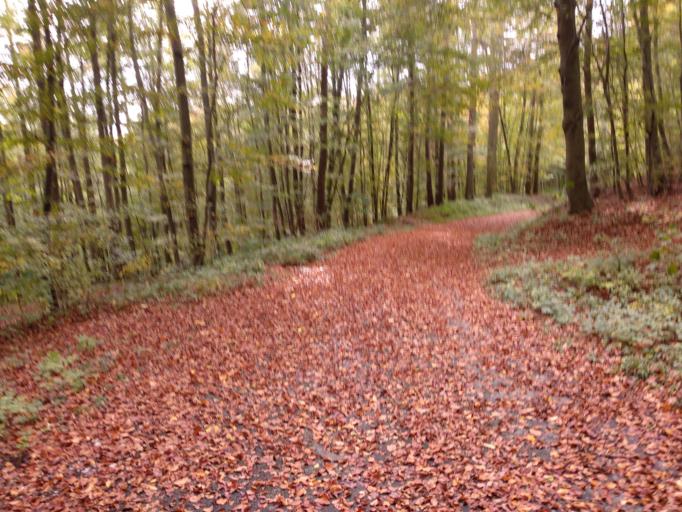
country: DE
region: North Rhine-Westphalia
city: Beverungen
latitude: 51.6633
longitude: 9.3497
